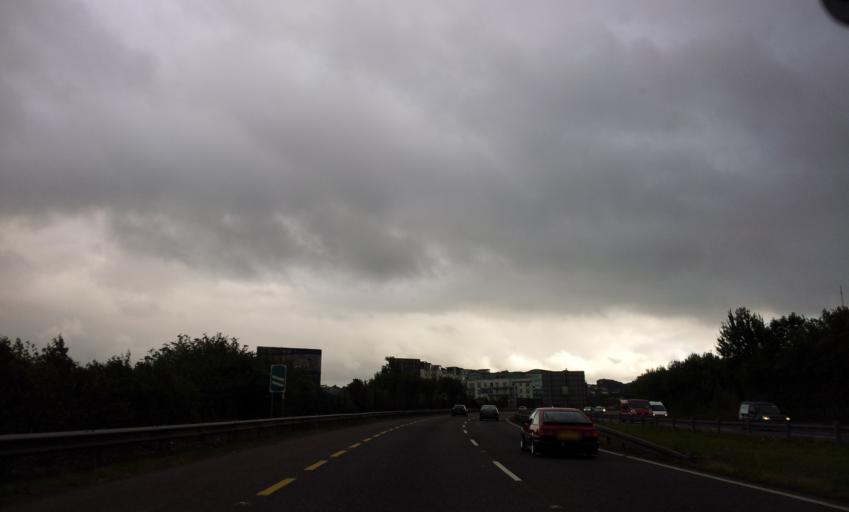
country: IE
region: Munster
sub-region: County Cork
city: Passage West
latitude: 51.8886
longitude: -8.3907
